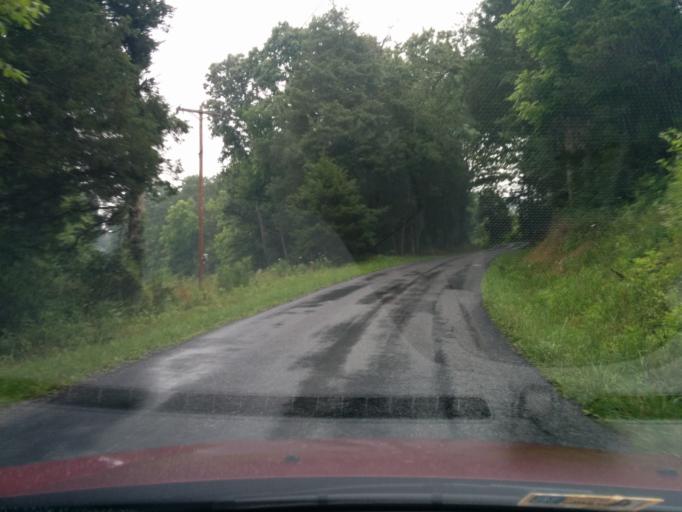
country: US
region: Virginia
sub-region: Rockbridge County
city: East Lexington
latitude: 37.8583
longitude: -79.4237
